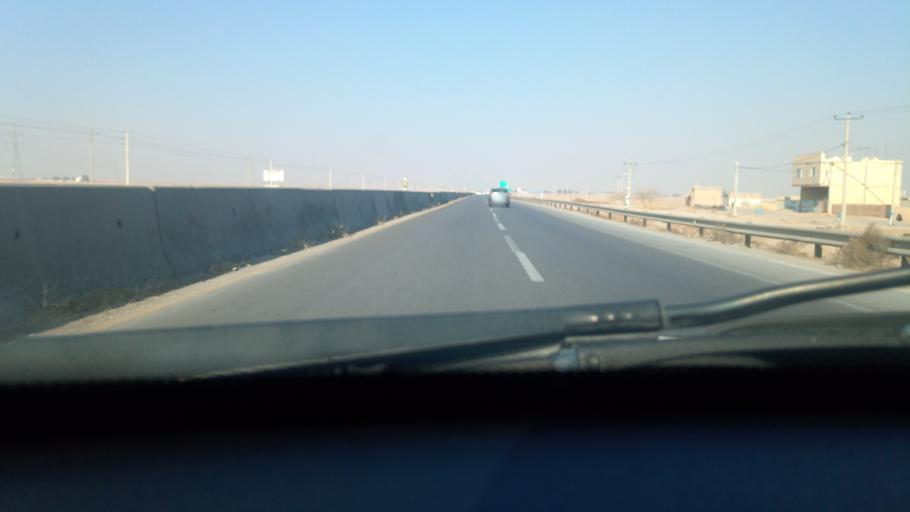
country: IR
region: Razavi Khorasan
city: Chenaran
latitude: 36.8131
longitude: 58.8396
